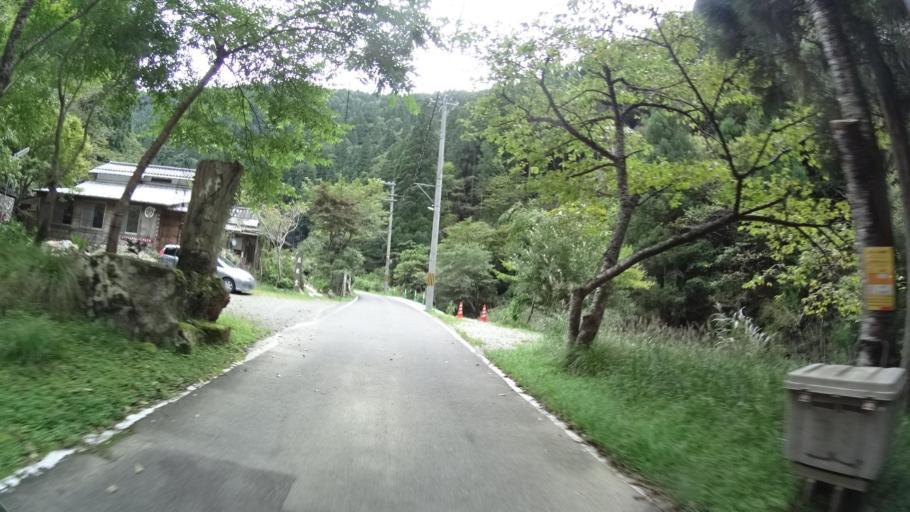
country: JP
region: Shiga Prefecture
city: Kitahama
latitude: 35.2348
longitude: 135.7856
